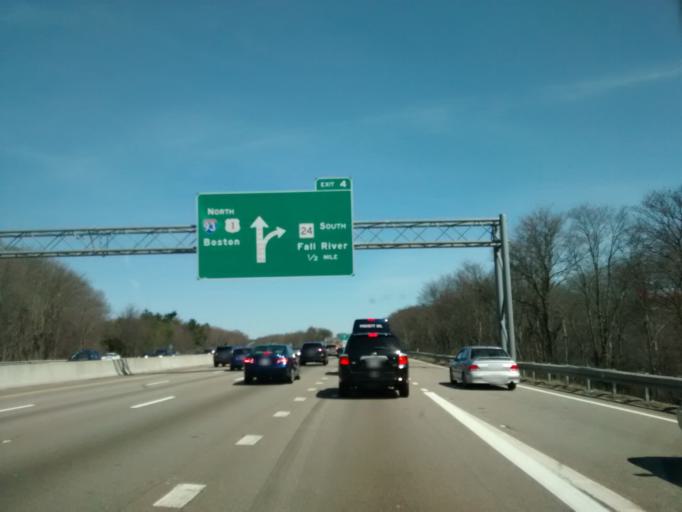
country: US
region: Massachusetts
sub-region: Norfolk County
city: Milton
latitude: 42.2027
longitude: -71.0928
